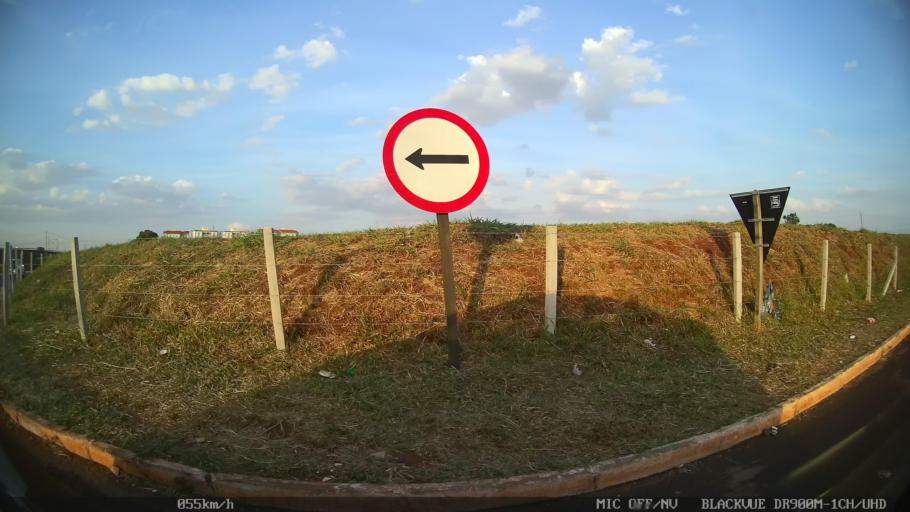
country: BR
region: Sao Paulo
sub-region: Ribeirao Preto
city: Ribeirao Preto
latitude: -21.1357
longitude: -47.8575
